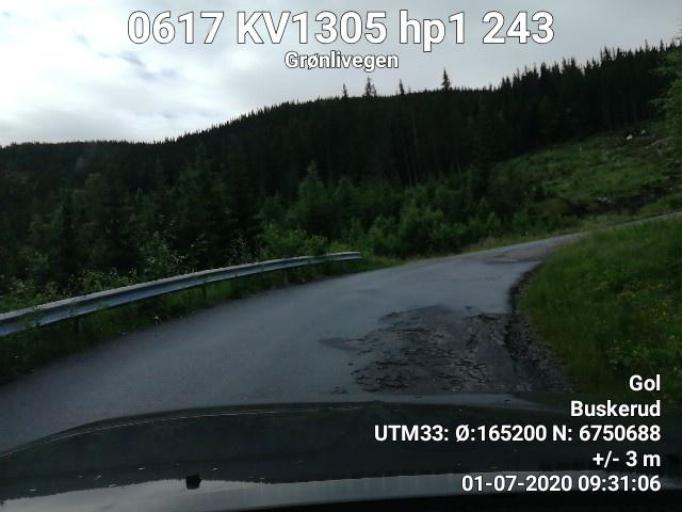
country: NO
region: Buskerud
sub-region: Gol
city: Gol
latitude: 60.7505
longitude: 8.8518
